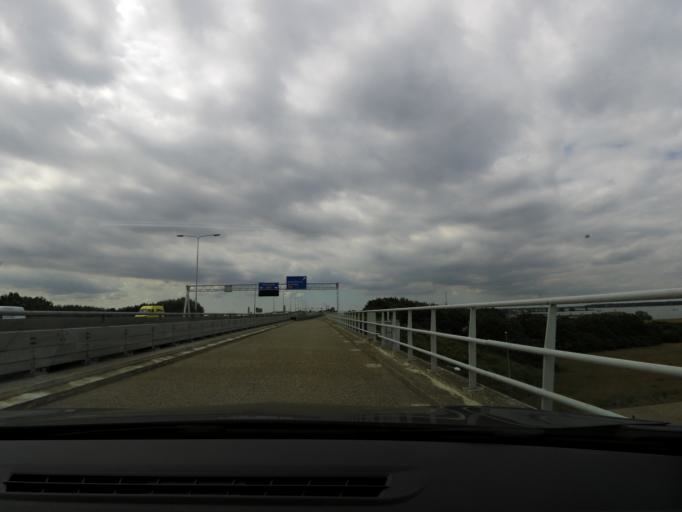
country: NL
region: North Brabant
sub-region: Gemeente Moerdijk
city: Willemstad
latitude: 51.6896
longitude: 4.4067
